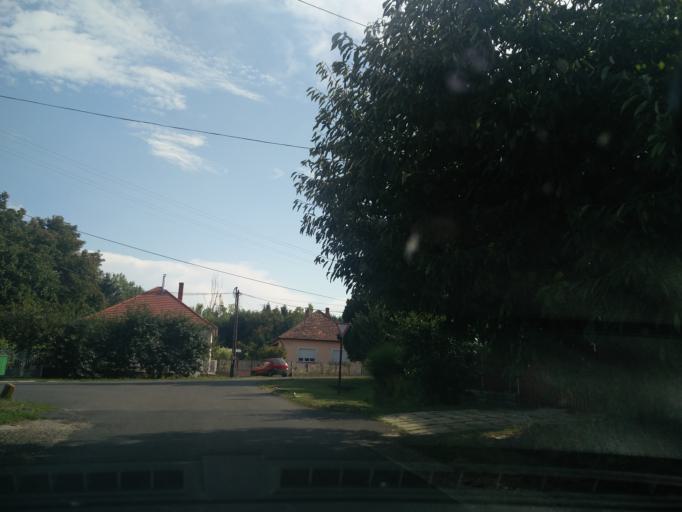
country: HU
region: Zala
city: Zalaegerszeg
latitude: 46.8467
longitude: 16.8176
